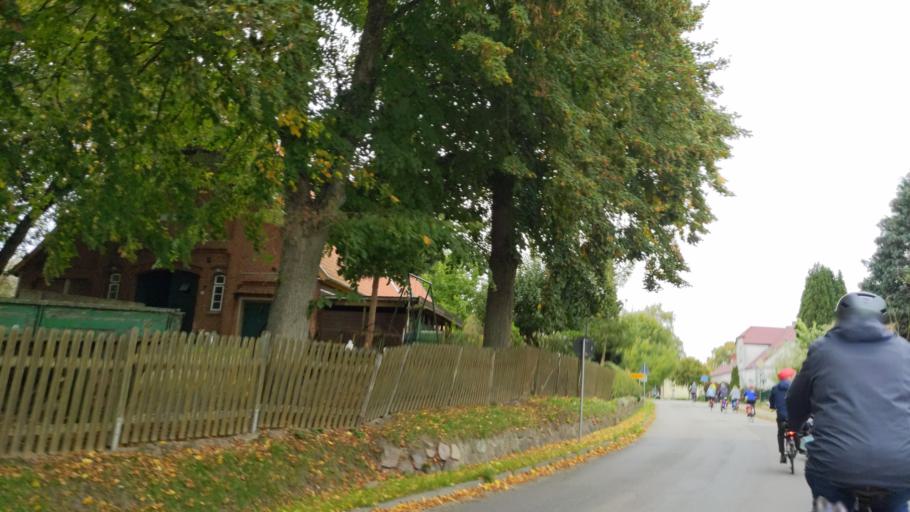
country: DE
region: Schleswig-Holstein
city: Gross Sarau
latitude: 53.7678
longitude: 10.7695
